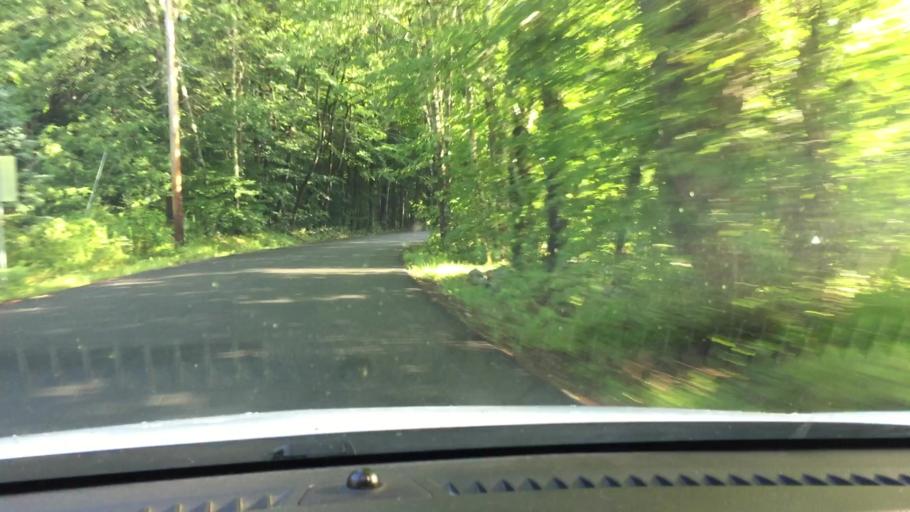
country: US
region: Massachusetts
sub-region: Berkshire County
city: Becket
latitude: 42.3815
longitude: -72.9781
